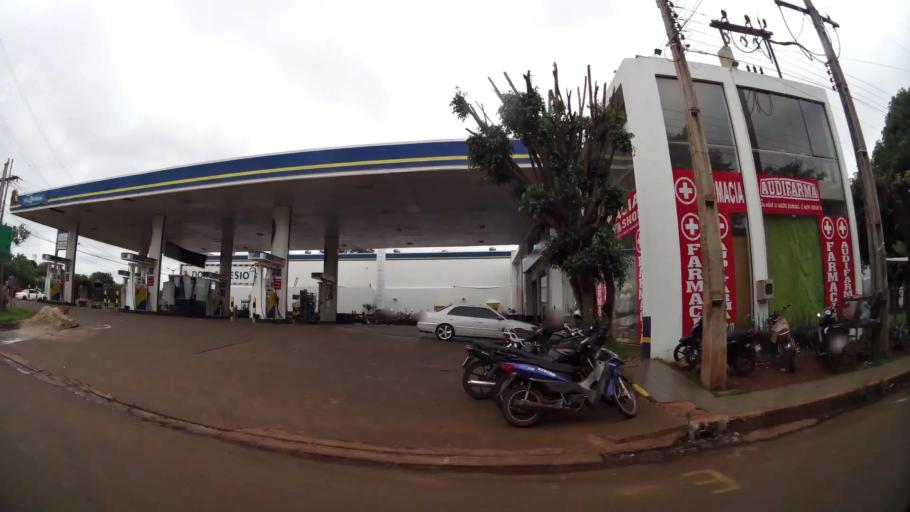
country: PY
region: Alto Parana
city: Ciudad del Este
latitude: -25.4965
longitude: -54.6874
